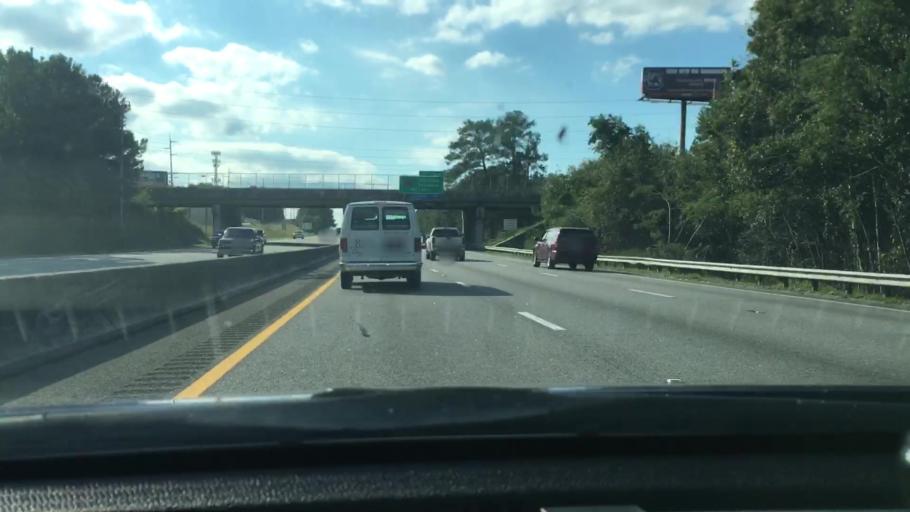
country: US
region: South Carolina
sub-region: Richland County
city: Dentsville
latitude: 34.0740
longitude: -80.9577
